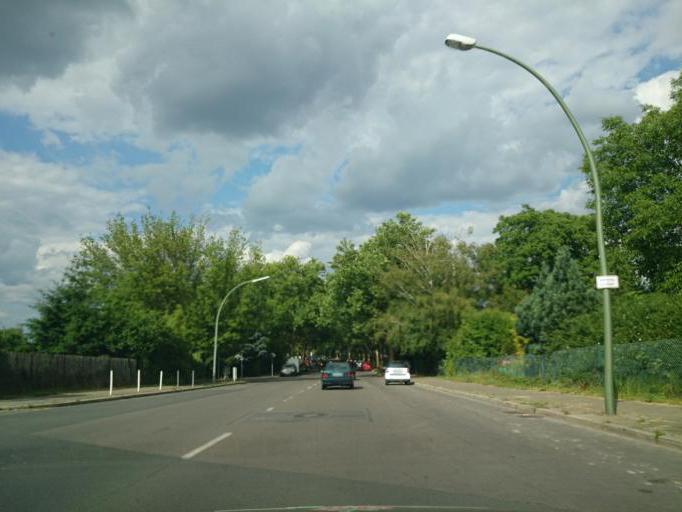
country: DE
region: Berlin
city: Marienfelde
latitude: 52.4148
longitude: 13.3819
